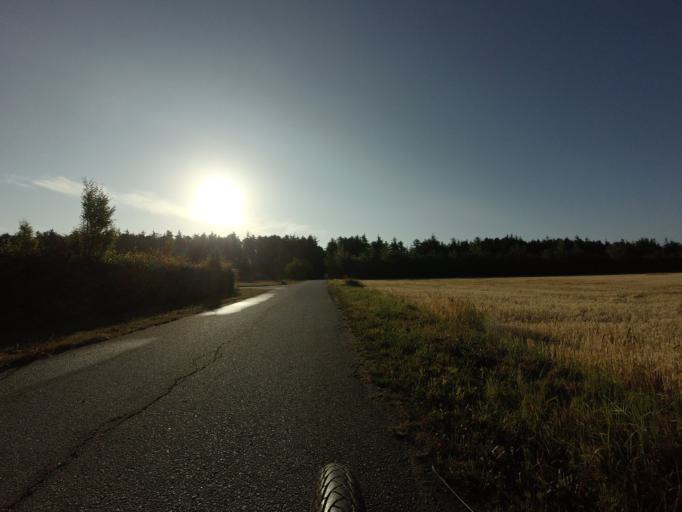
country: DK
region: North Denmark
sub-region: Hjorring Kommune
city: Vra
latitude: 57.3630
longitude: 9.8729
